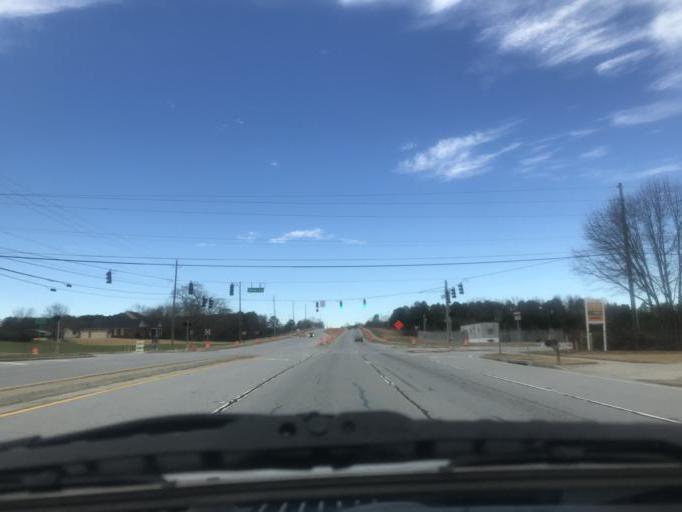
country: US
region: Georgia
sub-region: Gwinnett County
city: Dacula
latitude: 34.0604
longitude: -83.9436
